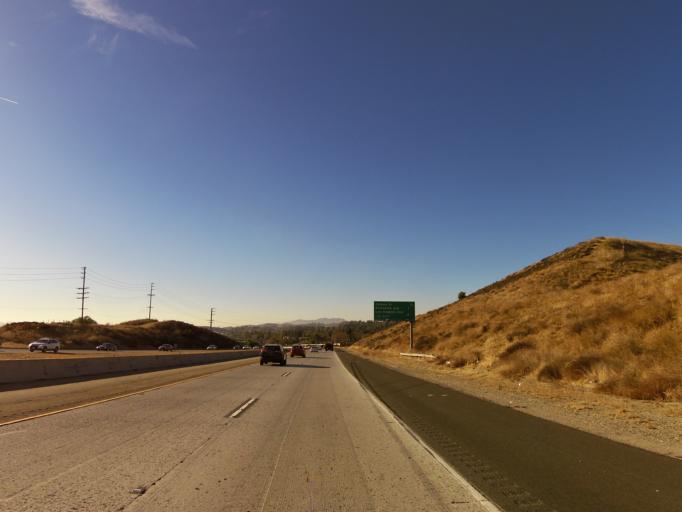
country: US
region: California
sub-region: Ventura County
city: Moorpark
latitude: 34.2926
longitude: -118.8325
